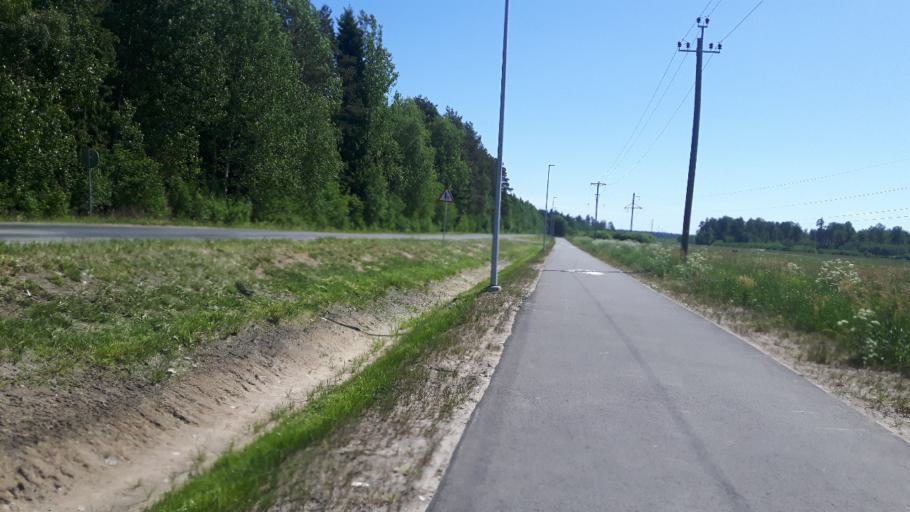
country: EE
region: Raplamaa
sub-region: Kohila vald
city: Kohila
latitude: 59.2116
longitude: 24.6819
